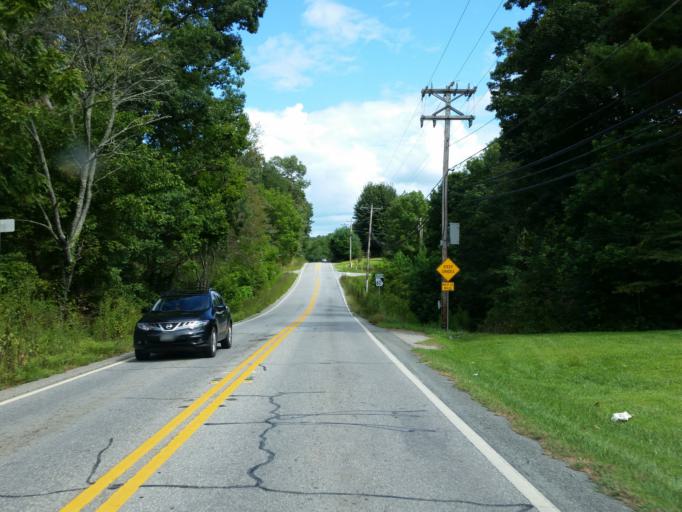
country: US
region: Georgia
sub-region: Fannin County
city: Blue Ridge
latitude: 34.8854
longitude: -84.2612
